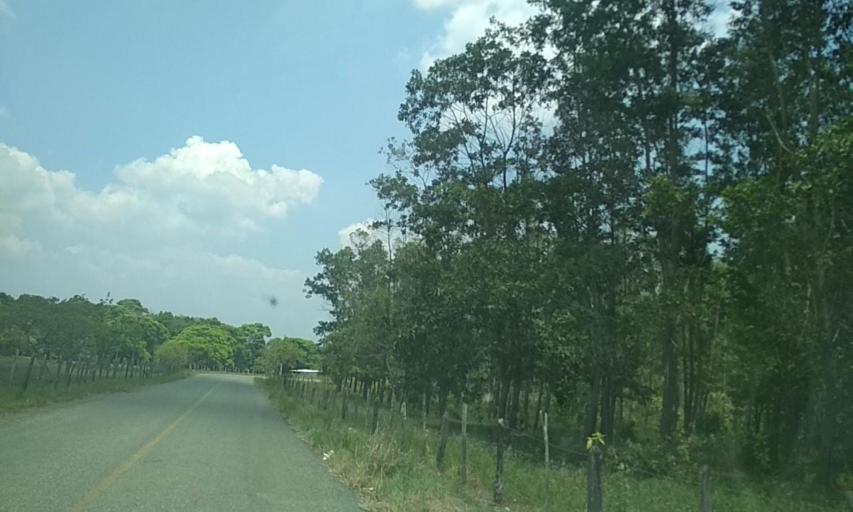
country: MX
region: Tabasco
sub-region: Huimanguillo
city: Francisco Rueda
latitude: 17.8379
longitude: -93.9104
